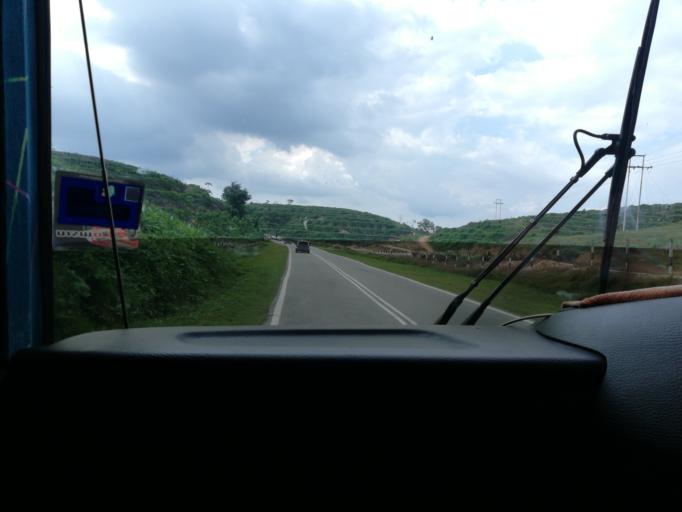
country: MY
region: Kedah
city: Kulim
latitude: 5.3070
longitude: 100.6140
